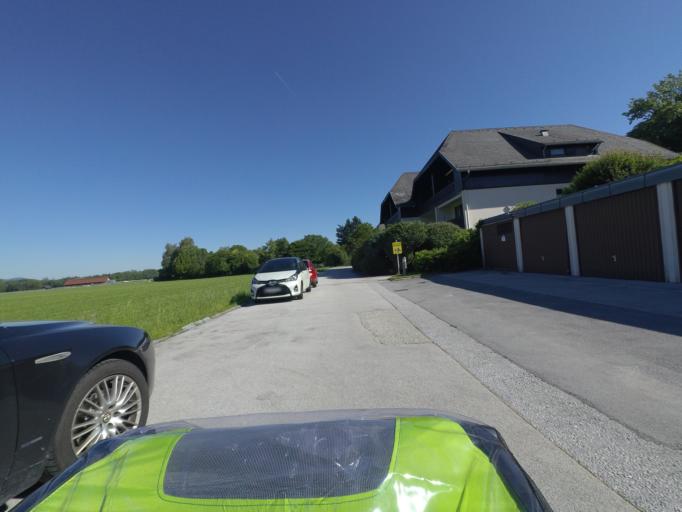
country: AT
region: Salzburg
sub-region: Politischer Bezirk Salzburg-Umgebung
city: Anif
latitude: 47.7485
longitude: 13.0582
